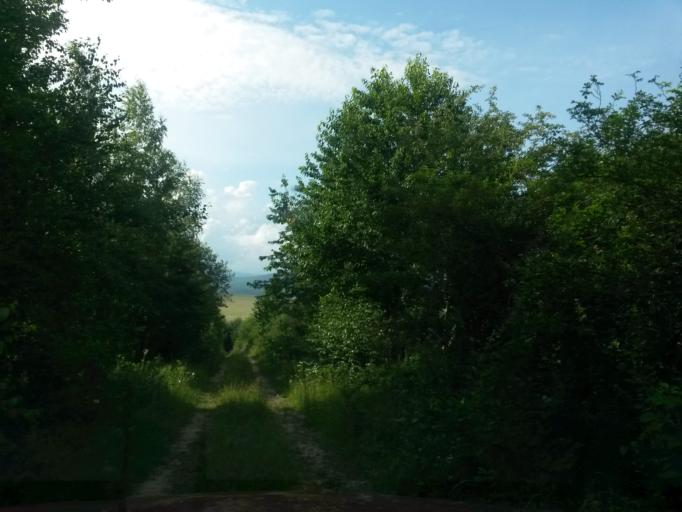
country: SK
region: Kosicky
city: Moldava nad Bodvou
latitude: 48.6470
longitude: 21.1093
